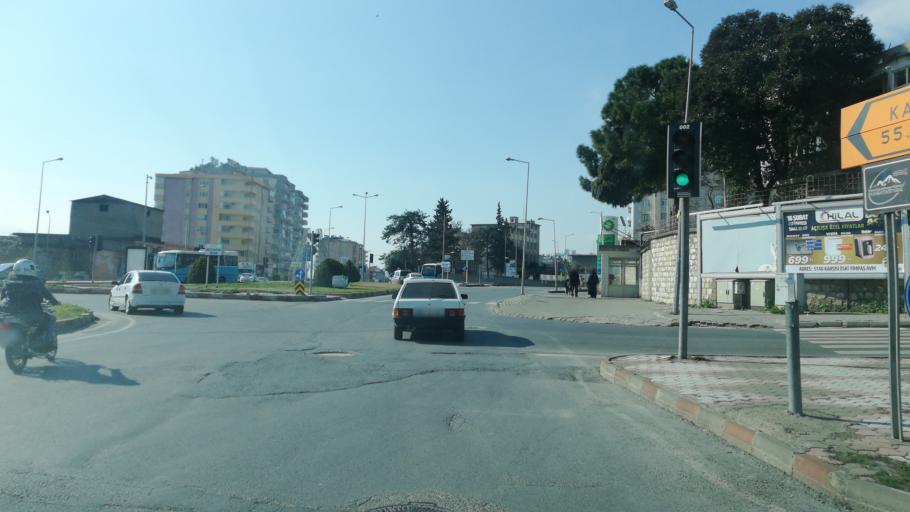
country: TR
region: Kahramanmaras
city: Kahramanmaras
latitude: 37.5714
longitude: 36.9430
